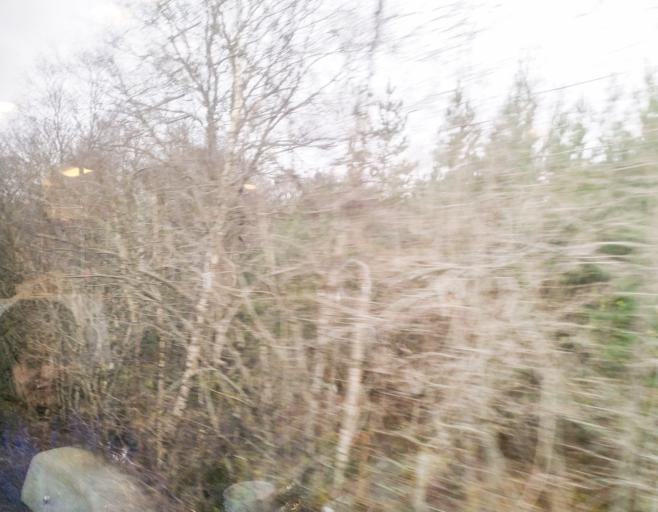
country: GB
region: Scotland
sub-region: Highland
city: Spean Bridge
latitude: 56.8894
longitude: -4.8712
